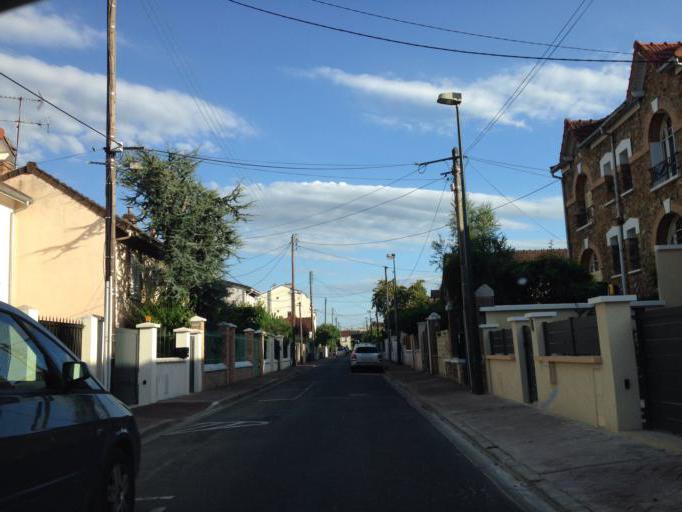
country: FR
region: Ile-de-France
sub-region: Departement des Hauts-de-Seine
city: Clamart
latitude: 48.7944
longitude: 2.2544
